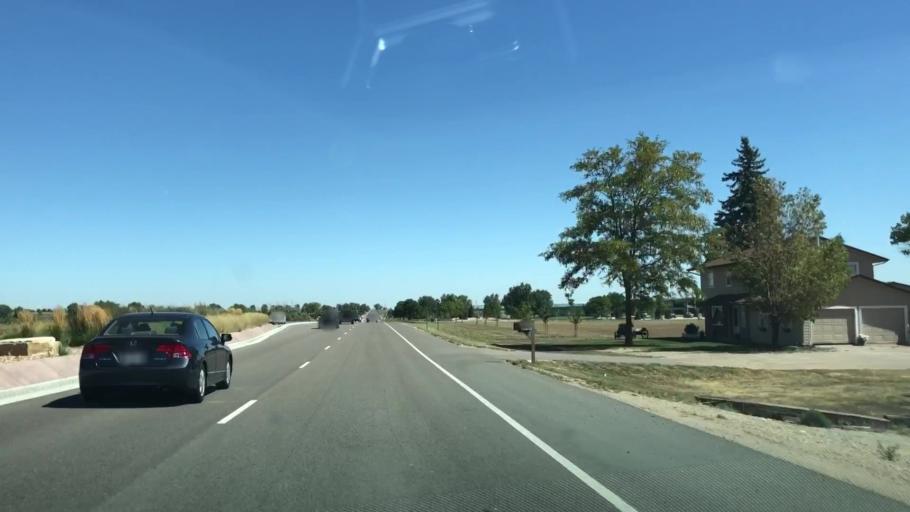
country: US
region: Colorado
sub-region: Weld County
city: Windsor
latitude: 40.5229
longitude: -104.9708
